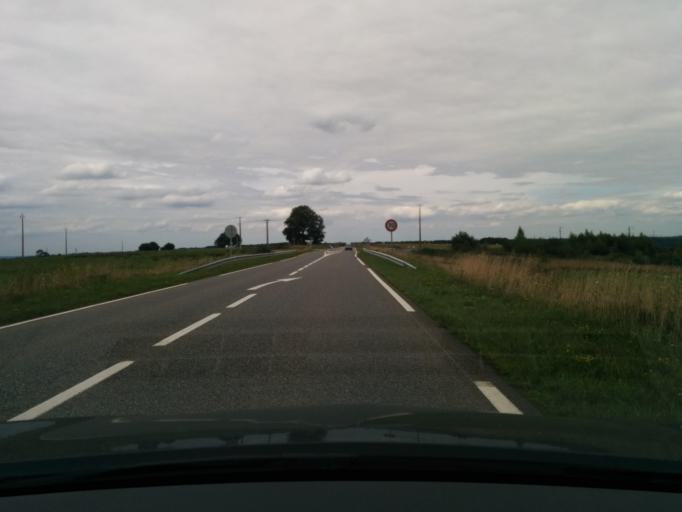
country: FR
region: Midi-Pyrenees
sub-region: Departement des Hautes-Pyrenees
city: La Barthe-de-Neste
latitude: 43.0477
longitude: 0.3625
